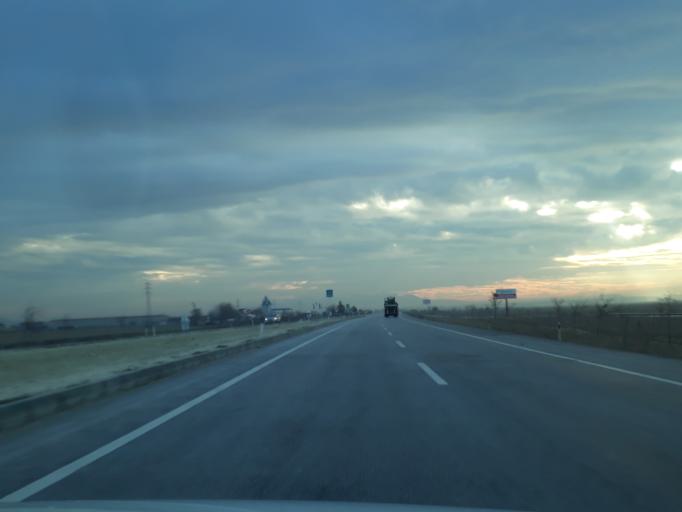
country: TR
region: Konya
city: Hotamis
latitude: 37.7124
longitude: 33.3798
